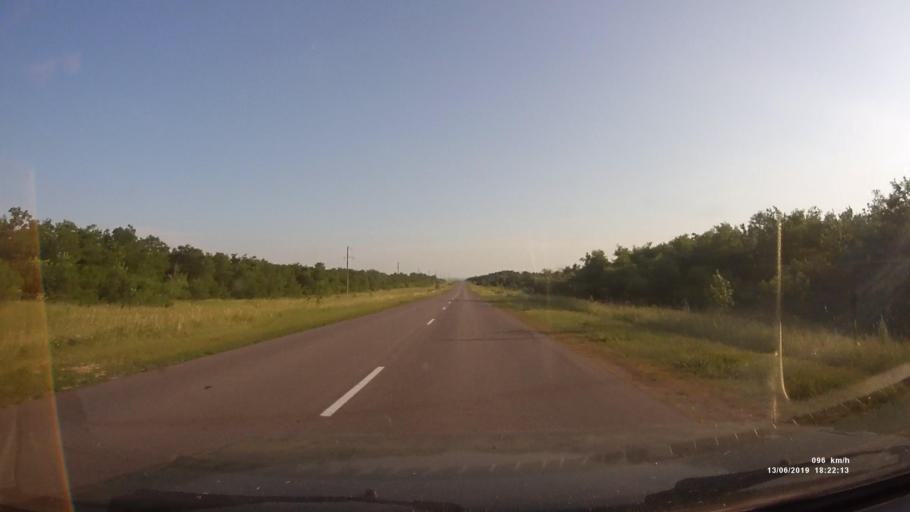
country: RU
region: Rostov
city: Kazanskaya
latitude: 49.8614
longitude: 41.2805
